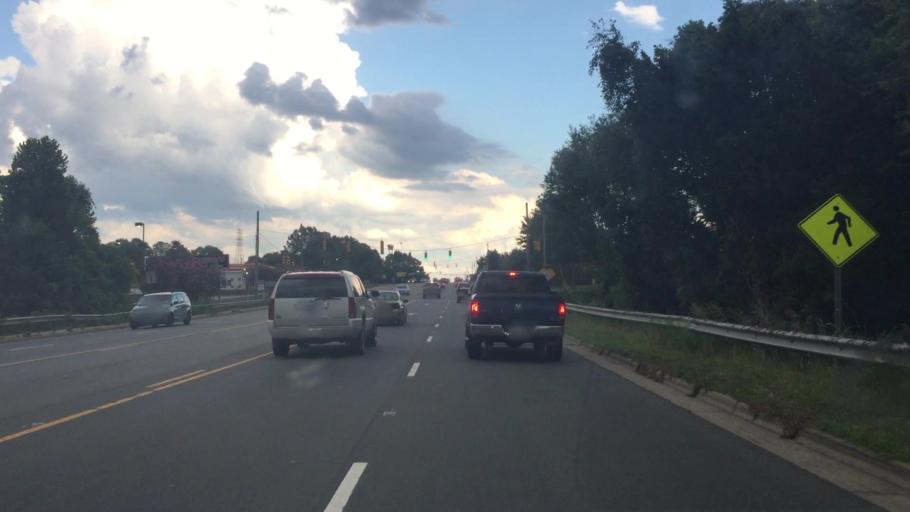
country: US
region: North Carolina
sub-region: Rowan County
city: Salisbury
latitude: 35.6449
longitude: -80.4869
